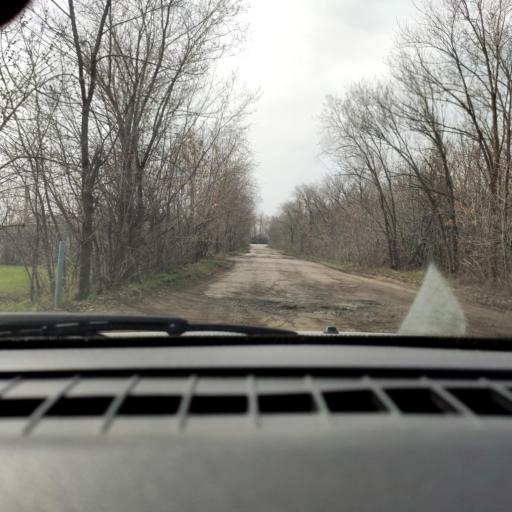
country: RU
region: Samara
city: Dubovyy Umet
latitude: 53.0917
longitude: 50.3051
